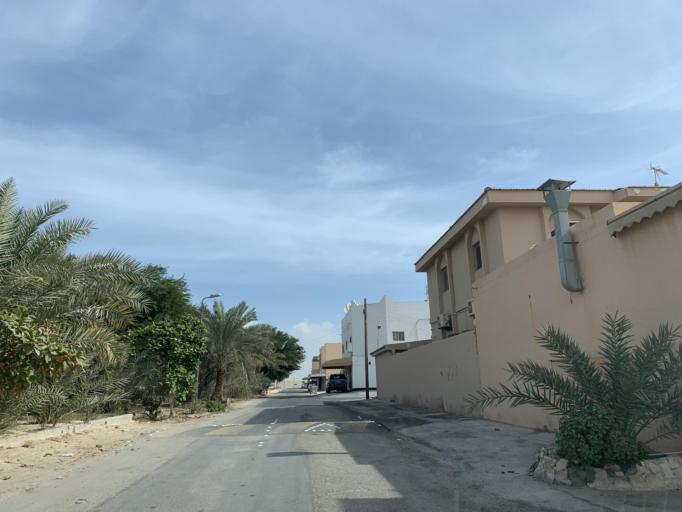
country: BH
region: Central Governorate
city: Madinat Hamad
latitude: 26.1309
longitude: 50.4757
